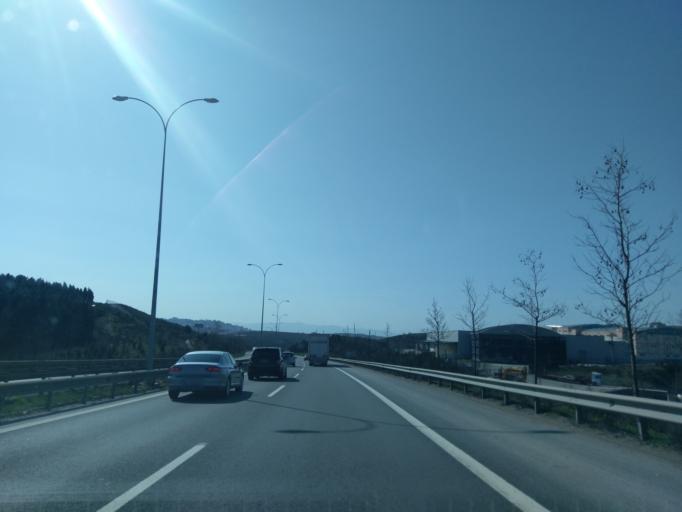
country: TR
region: Kocaeli
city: Balcik
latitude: 40.8518
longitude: 29.3749
